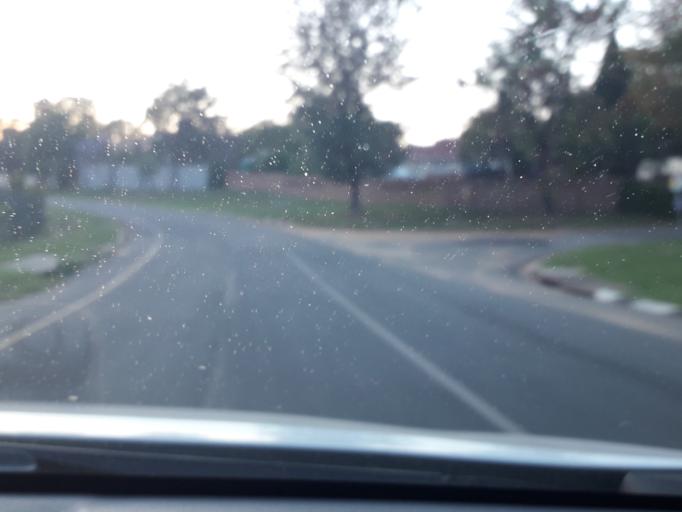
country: ZA
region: Gauteng
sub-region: City of Johannesburg Metropolitan Municipality
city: Modderfontein
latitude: -26.1226
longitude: 28.1012
